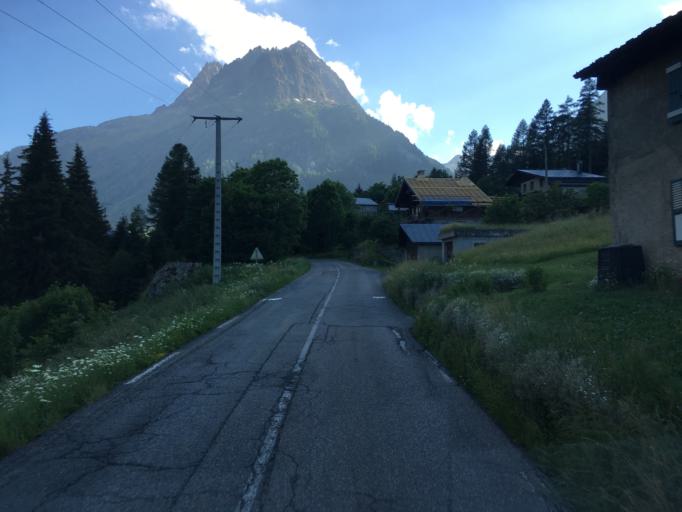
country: FR
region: Rhone-Alpes
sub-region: Departement de la Haute-Savoie
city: Chamonix-Mont-Blanc
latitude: 46.0294
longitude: 6.9278
